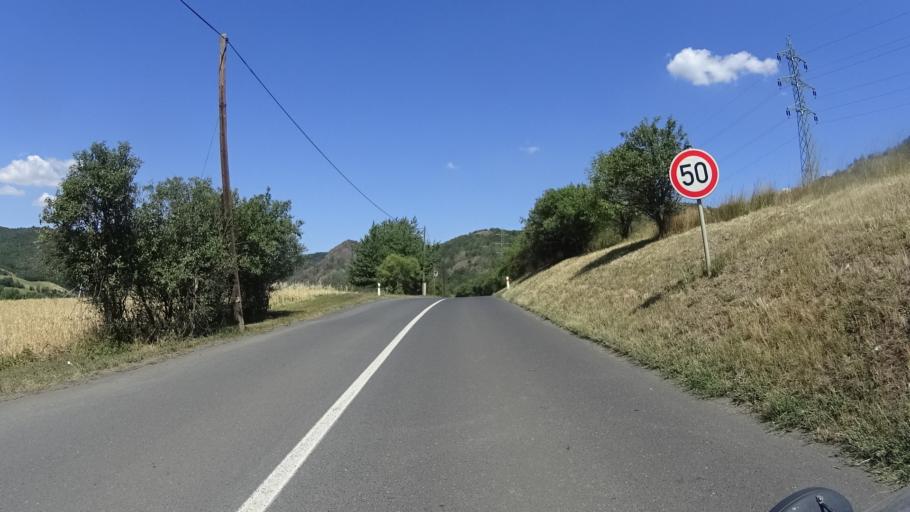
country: CZ
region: Ustecky
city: Lovosice
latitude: 50.5757
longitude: 14.0450
